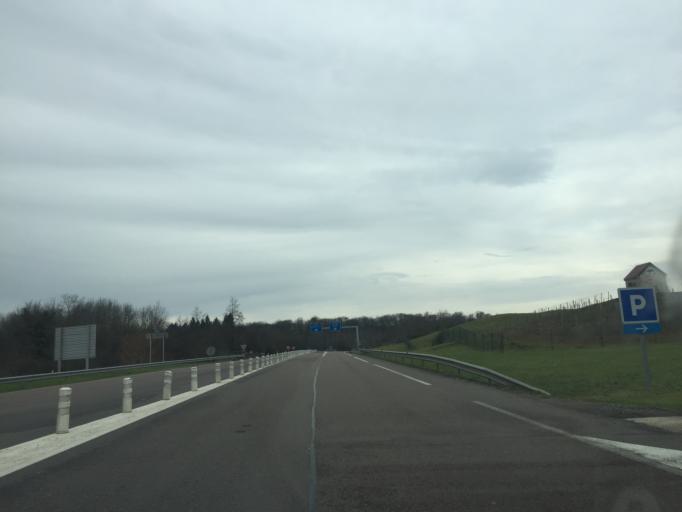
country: FR
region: Franche-Comte
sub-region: Departement du Jura
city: Poligny
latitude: 46.8499
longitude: 5.5740
